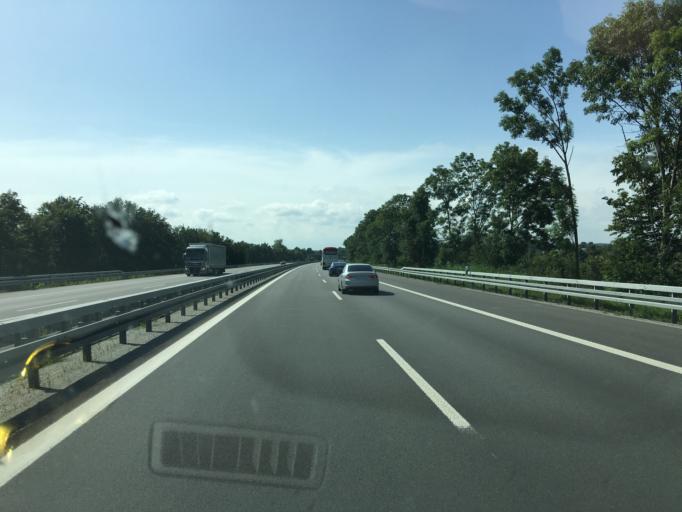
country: AT
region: Upper Austria
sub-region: Politischer Bezirk Scharding
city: Sankt Florian am Inn
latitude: 48.4187
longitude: 13.4020
